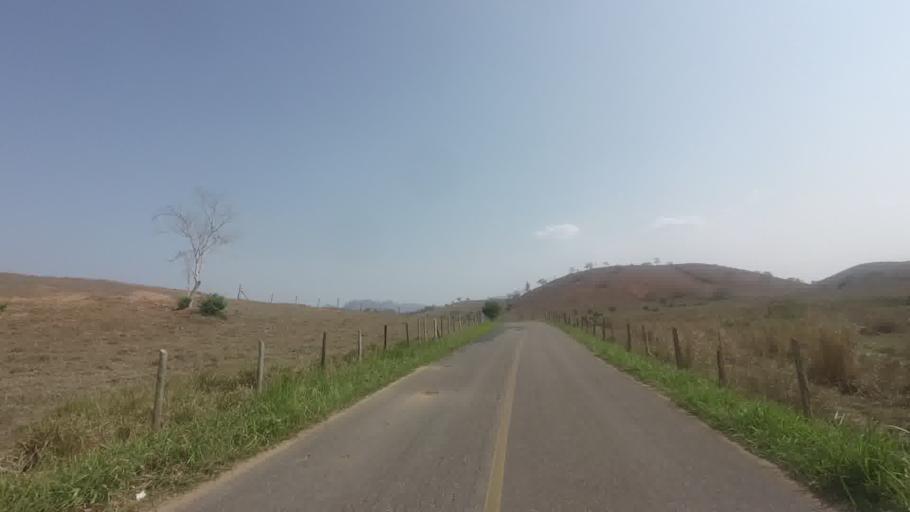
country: BR
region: Rio de Janeiro
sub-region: Bom Jesus Do Itabapoana
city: Bom Jesus do Itabapoana
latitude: -21.1291
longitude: -41.5674
